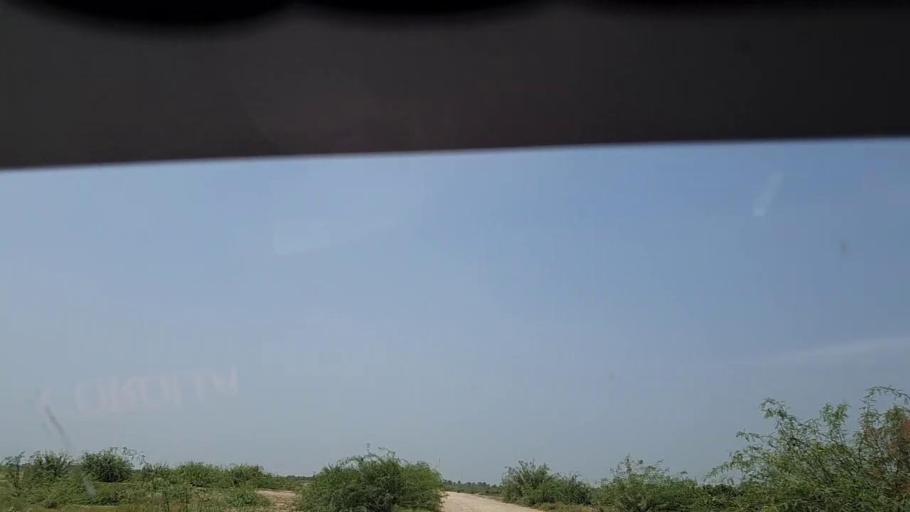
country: PK
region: Sindh
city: Adilpur
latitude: 27.9066
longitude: 69.2221
